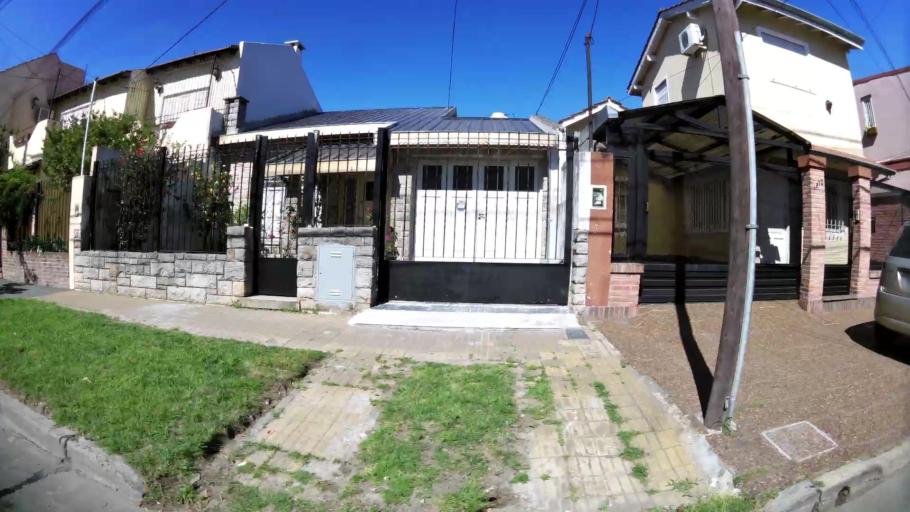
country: AR
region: Buenos Aires
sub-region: Partido de General San Martin
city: General San Martin
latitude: -34.5400
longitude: -58.5113
